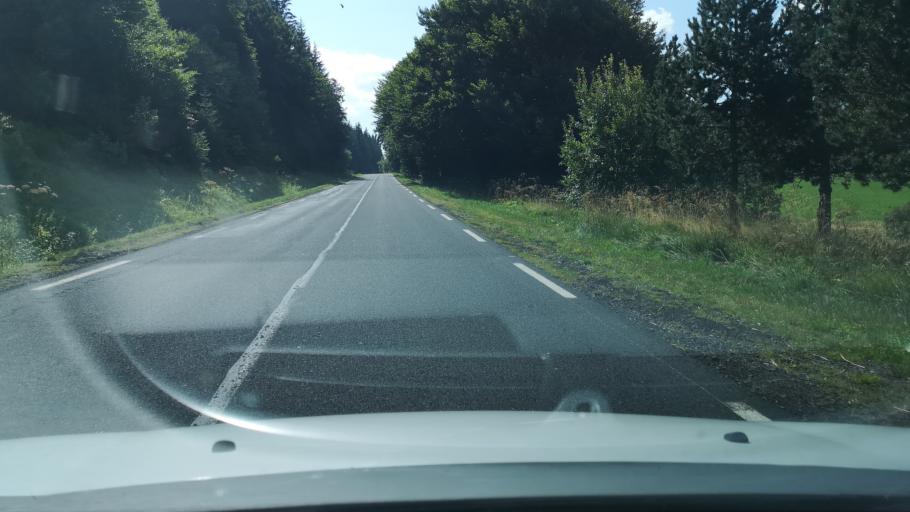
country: FR
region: Auvergne
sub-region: Departement du Puy-de-Dome
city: Mont-Dore
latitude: 45.4952
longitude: 2.8731
